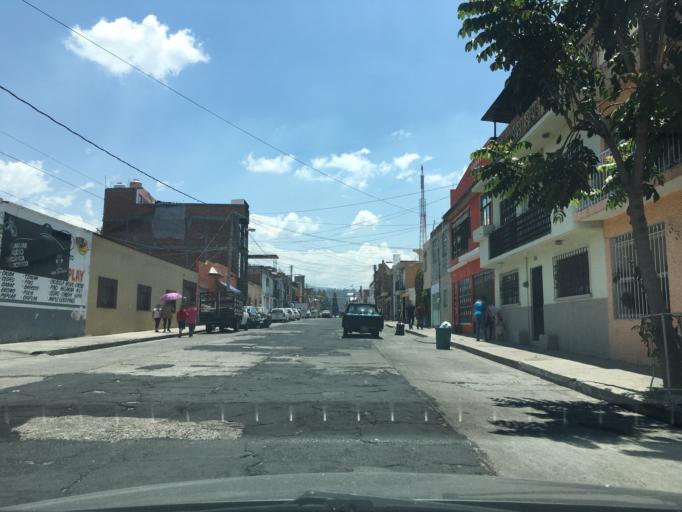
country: MX
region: Michoacan
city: Morelia
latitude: 19.7012
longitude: -101.1711
